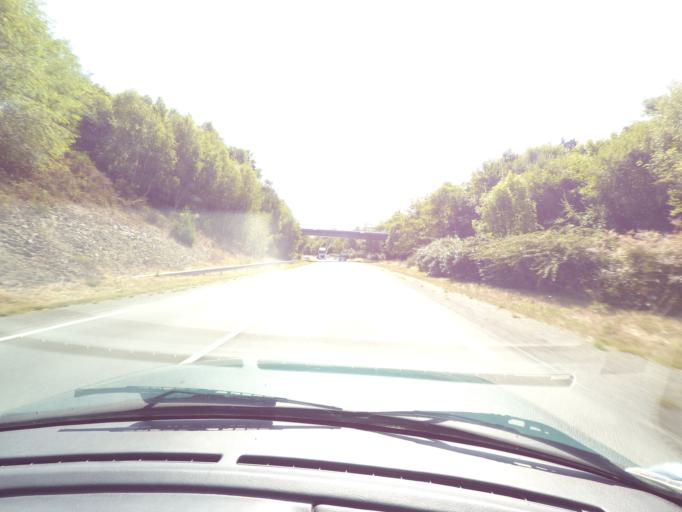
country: FR
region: Limousin
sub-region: Departement de la Haute-Vienne
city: Chaptelat
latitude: 45.8936
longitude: 1.2496
